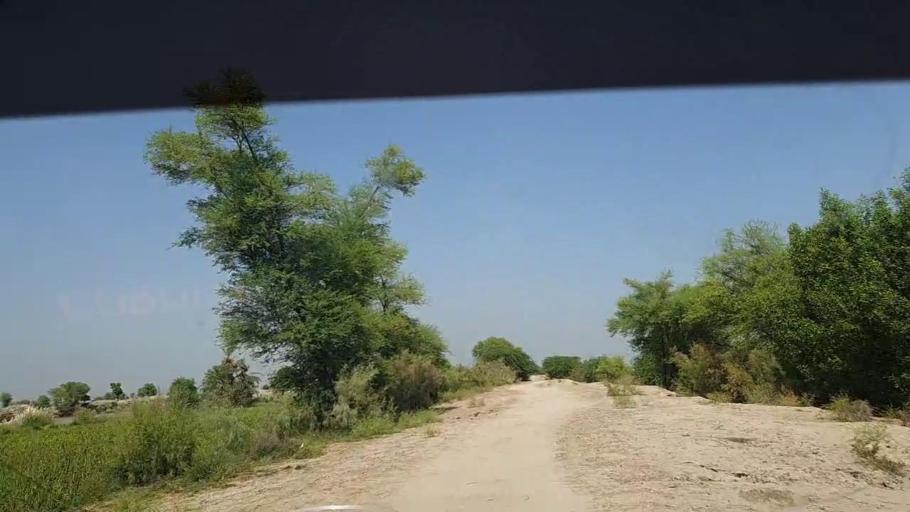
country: PK
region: Sindh
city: Ghauspur
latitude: 28.1733
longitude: 69.1458
